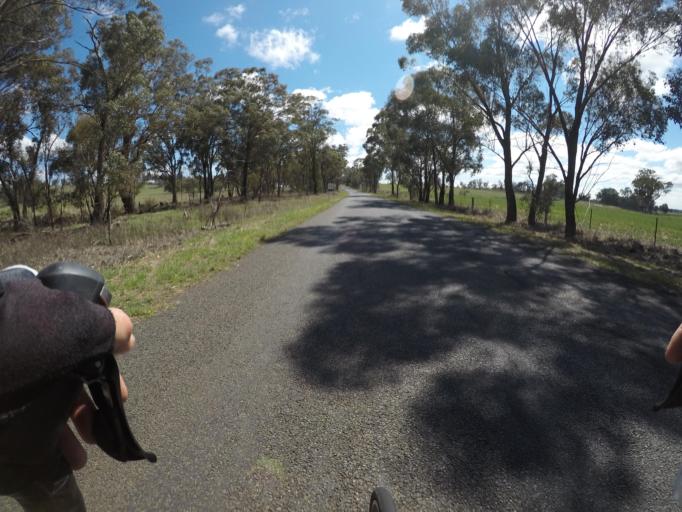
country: AU
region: New South Wales
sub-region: Dubbo Municipality
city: Dubbo
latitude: -32.5218
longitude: 148.5539
